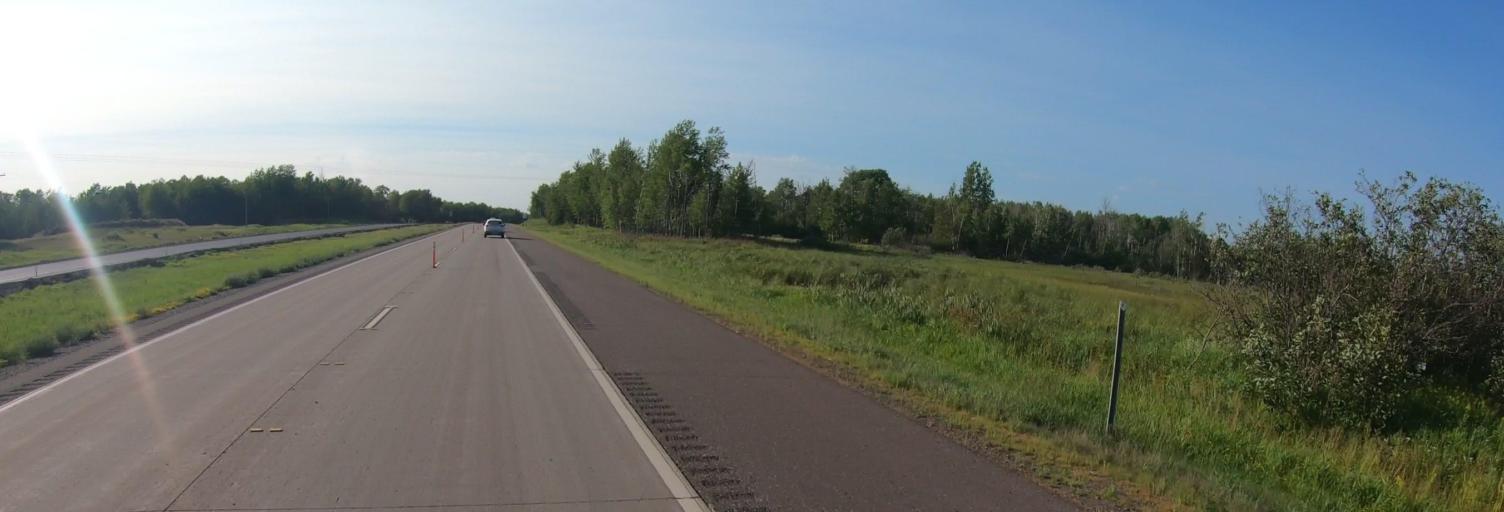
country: US
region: Minnesota
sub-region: Saint Louis County
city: Hermantown
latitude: 46.9133
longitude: -92.3935
